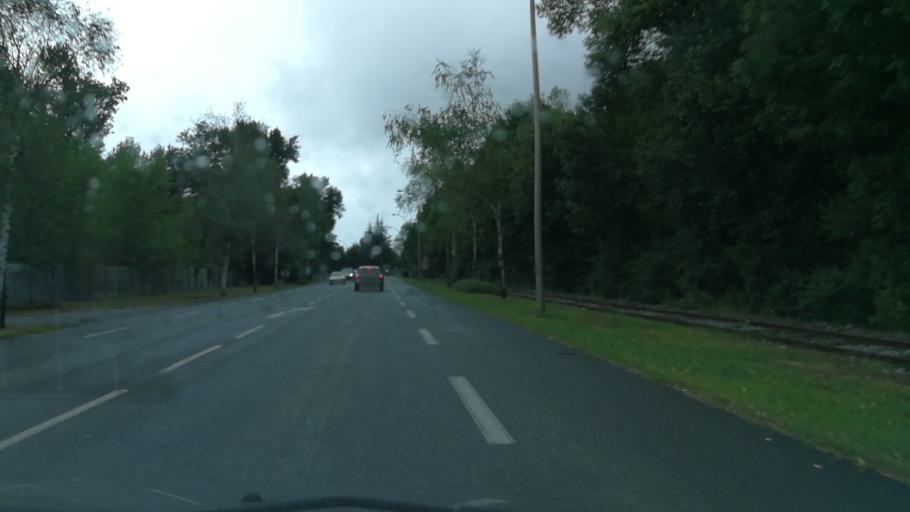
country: FR
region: Aquitaine
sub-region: Departement des Pyrenees-Atlantiques
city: Mourenx
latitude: 43.3889
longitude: -0.5815
